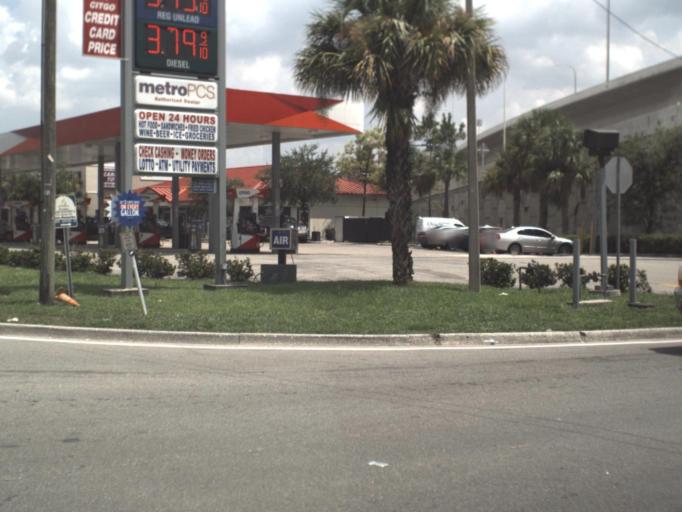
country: US
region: Florida
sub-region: Hillsborough County
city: Tampa
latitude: 27.9558
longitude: -82.4380
